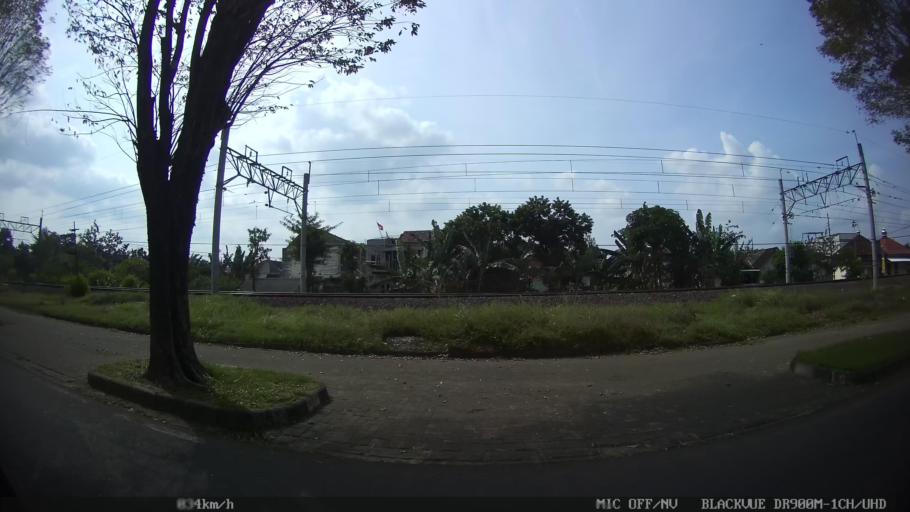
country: ID
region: Daerah Istimewa Yogyakarta
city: Depok
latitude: -7.7850
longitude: 110.4408
